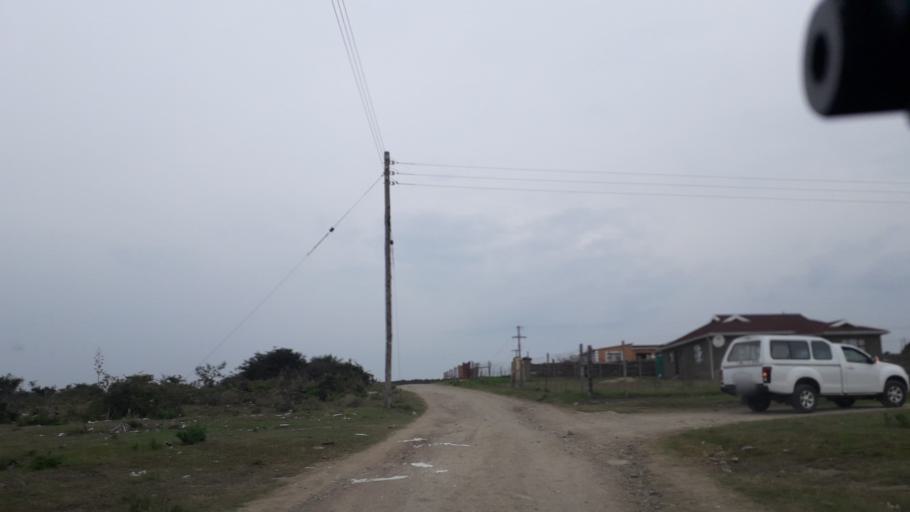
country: ZA
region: Eastern Cape
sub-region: Buffalo City Metropolitan Municipality
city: Bhisho
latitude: -32.8357
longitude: 27.3721
